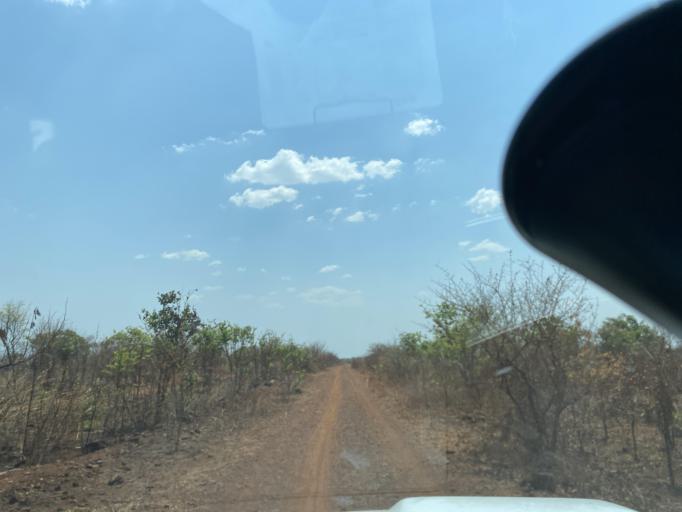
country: ZM
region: Lusaka
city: Lusaka
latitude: -15.4979
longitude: 27.9615
